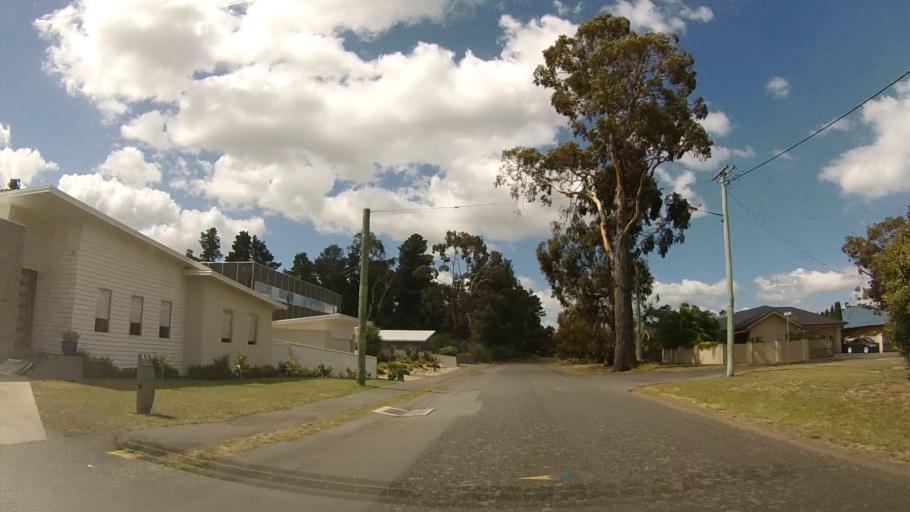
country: AU
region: Tasmania
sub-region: Clarence
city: Seven Mile Beach
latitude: -42.8556
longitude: 147.5050
